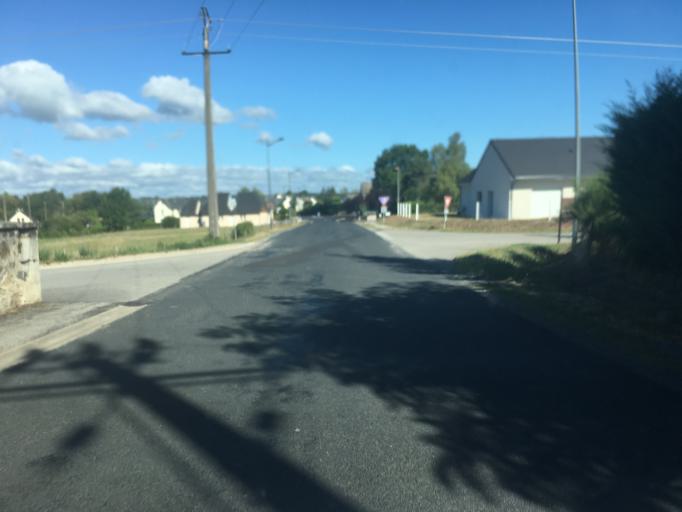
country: FR
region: Auvergne
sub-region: Departement du Cantal
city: Lanobre
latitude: 45.4379
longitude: 2.5288
